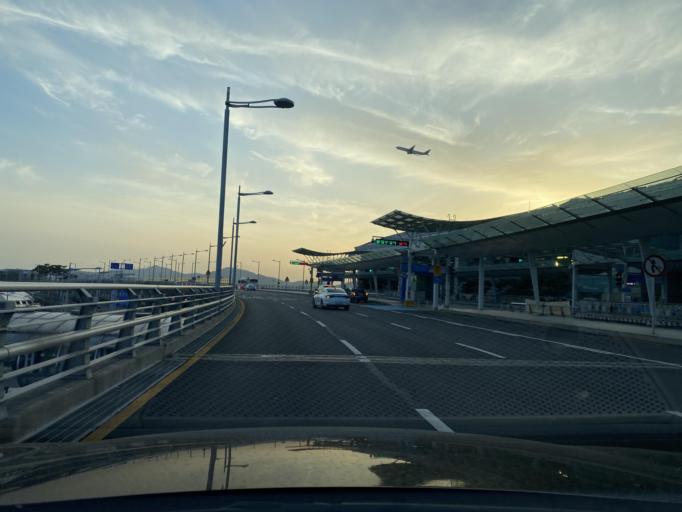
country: KR
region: Incheon
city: Incheon
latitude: 37.4479
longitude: 126.4506
